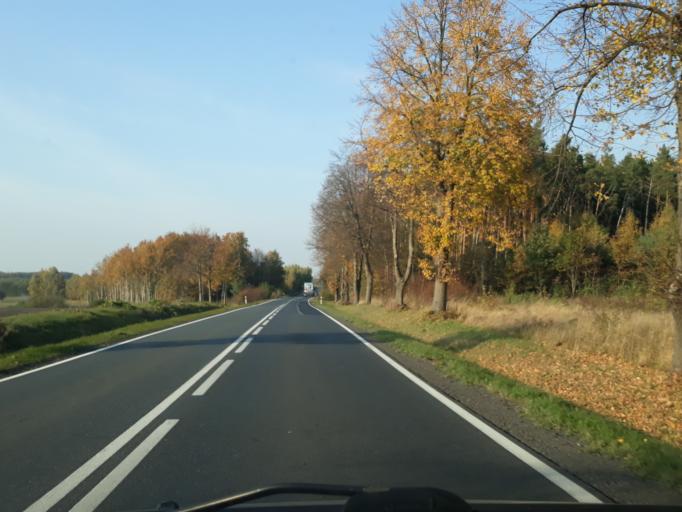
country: PL
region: Kujawsko-Pomorskie
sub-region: Powiat sepolenski
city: Sepolno Krajenskie
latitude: 53.4784
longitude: 17.5224
